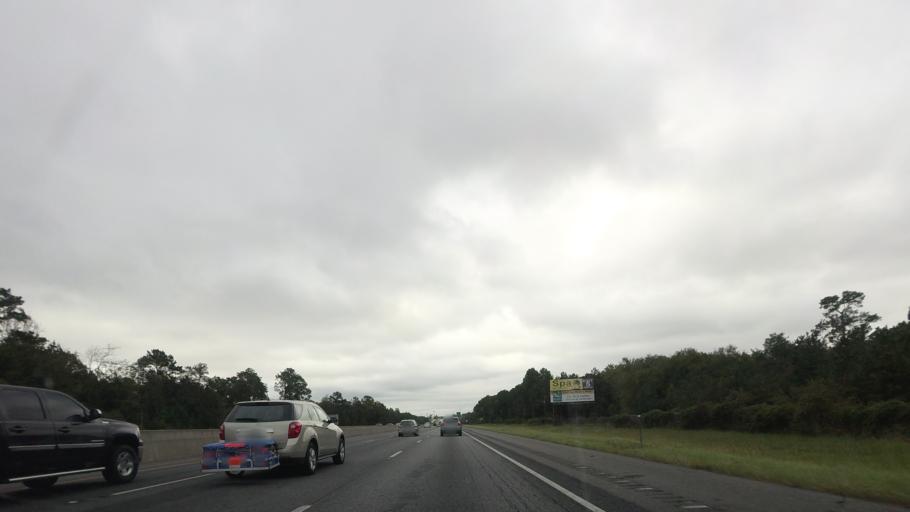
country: US
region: Georgia
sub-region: Lowndes County
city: Remerton
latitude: 30.8649
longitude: -83.3380
